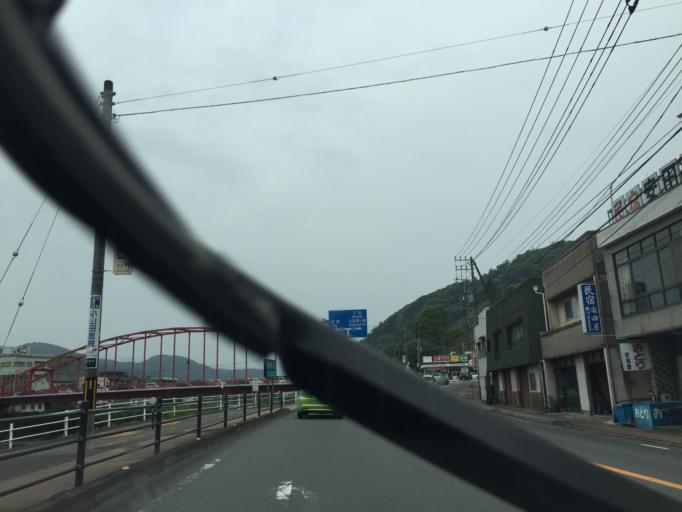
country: JP
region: Shizuoka
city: Ito
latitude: 34.9811
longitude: 138.9486
